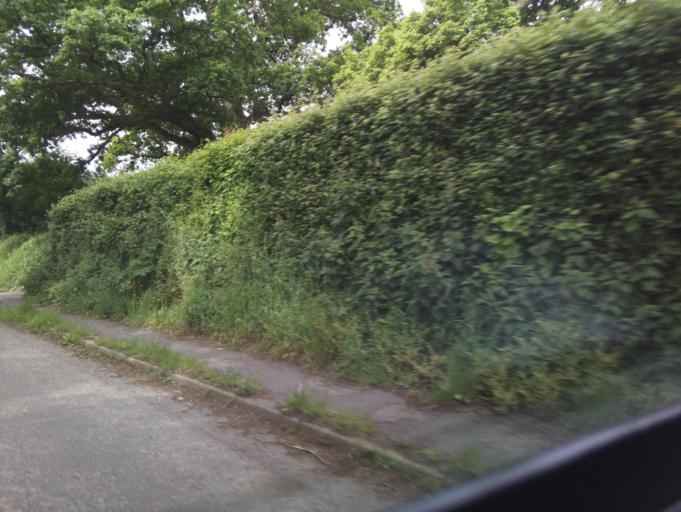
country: GB
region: England
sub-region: Devon
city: Chudleigh
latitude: 50.6174
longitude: -3.5846
